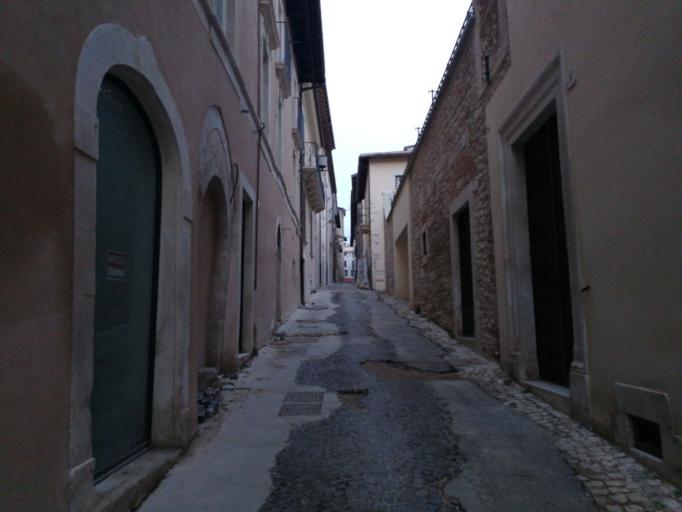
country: IT
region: Abruzzo
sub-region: Provincia dell' Aquila
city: L'Aquila
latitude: 42.3512
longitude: 13.3990
